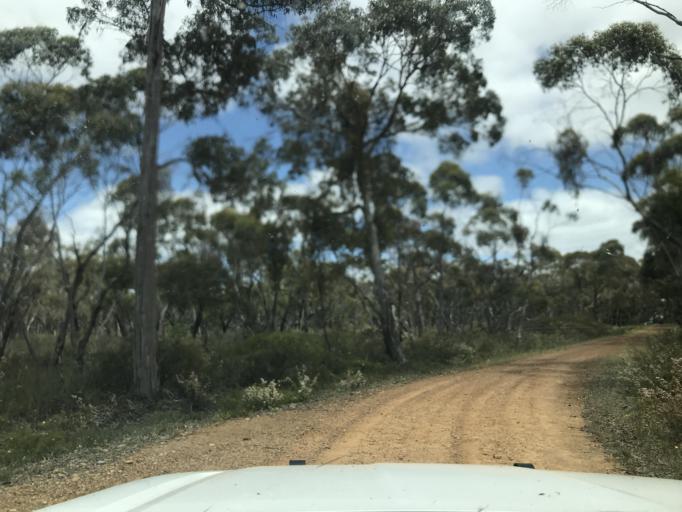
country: AU
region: South Australia
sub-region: Wattle Range
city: Penola
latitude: -37.3622
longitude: 141.1140
